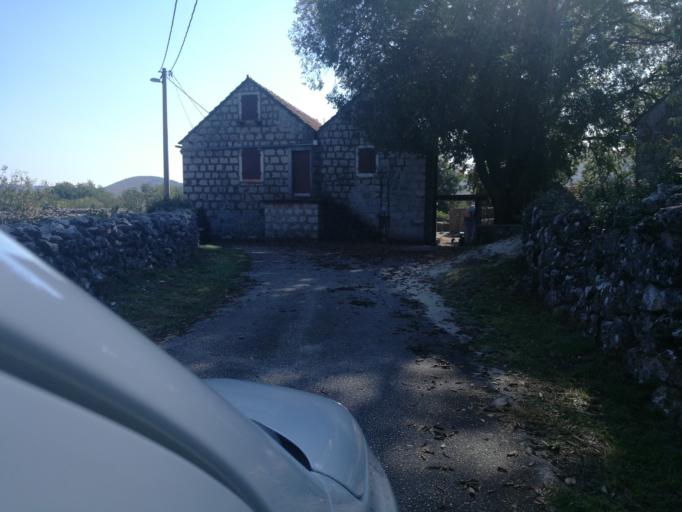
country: HR
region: Splitsko-Dalmatinska
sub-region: Grad Omis
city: Omis
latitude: 43.5203
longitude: 16.7486
